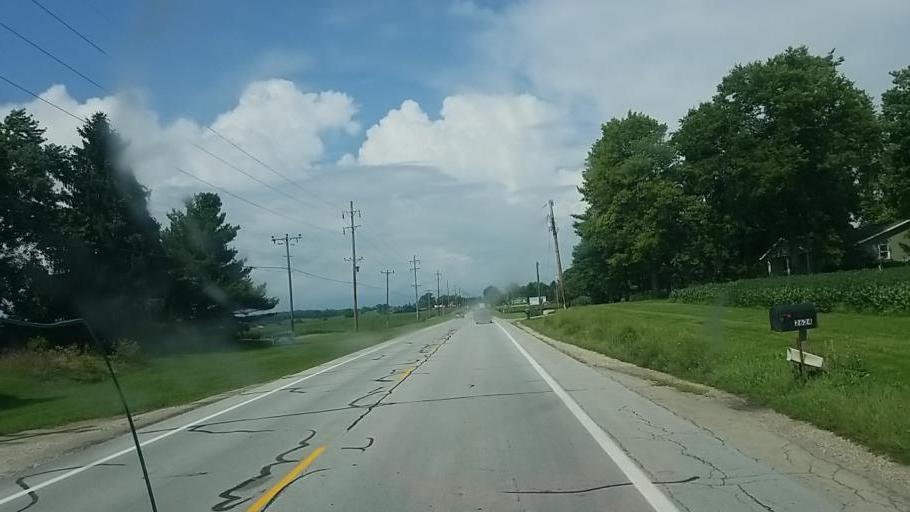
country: US
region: Ohio
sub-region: Champaign County
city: Urbana
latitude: 40.1480
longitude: -83.7464
